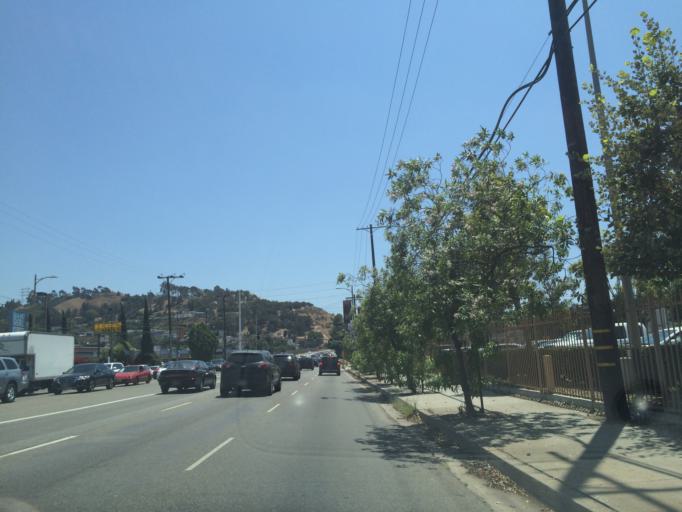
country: US
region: California
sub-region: Los Angeles County
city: Culver City
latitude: 34.0235
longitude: -118.3726
